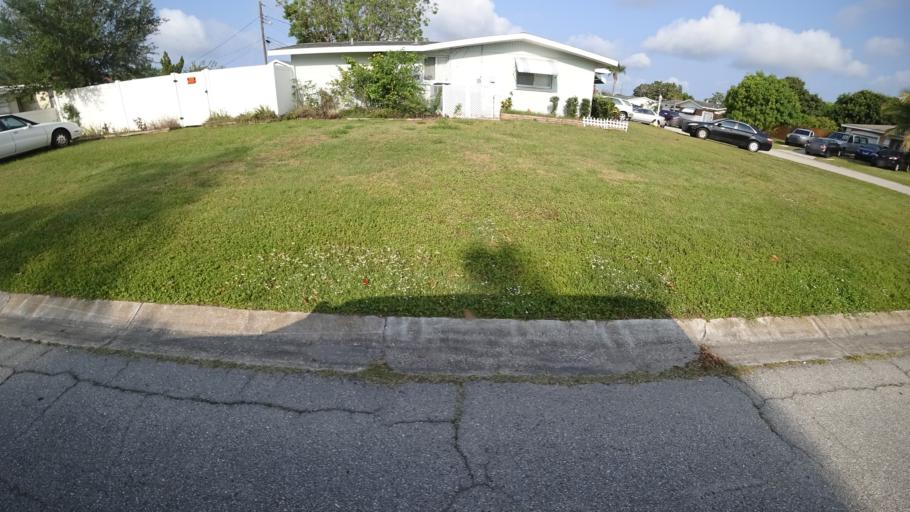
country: US
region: Florida
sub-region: Manatee County
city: South Bradenton
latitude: 27.4568
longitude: -82.5701
